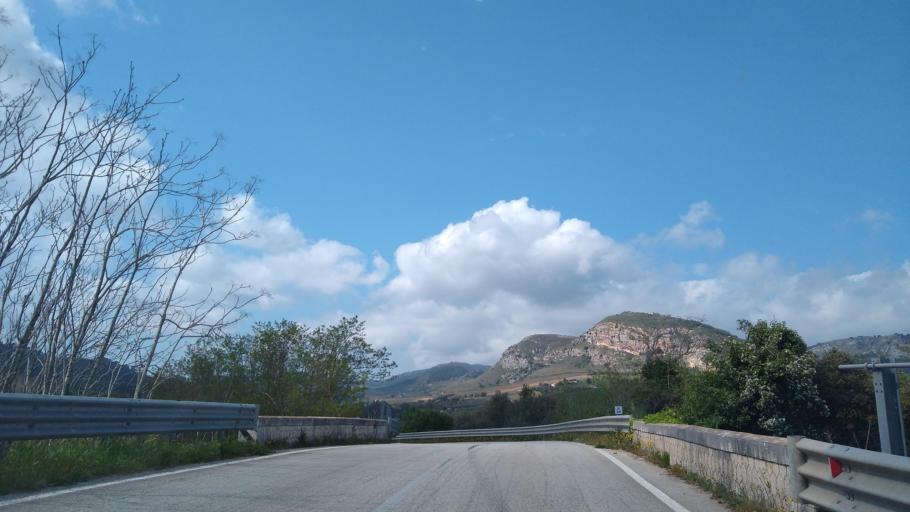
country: IT
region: Sicily
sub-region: Trapani
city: Calatafimi
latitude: 37.9498
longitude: 12.8619
